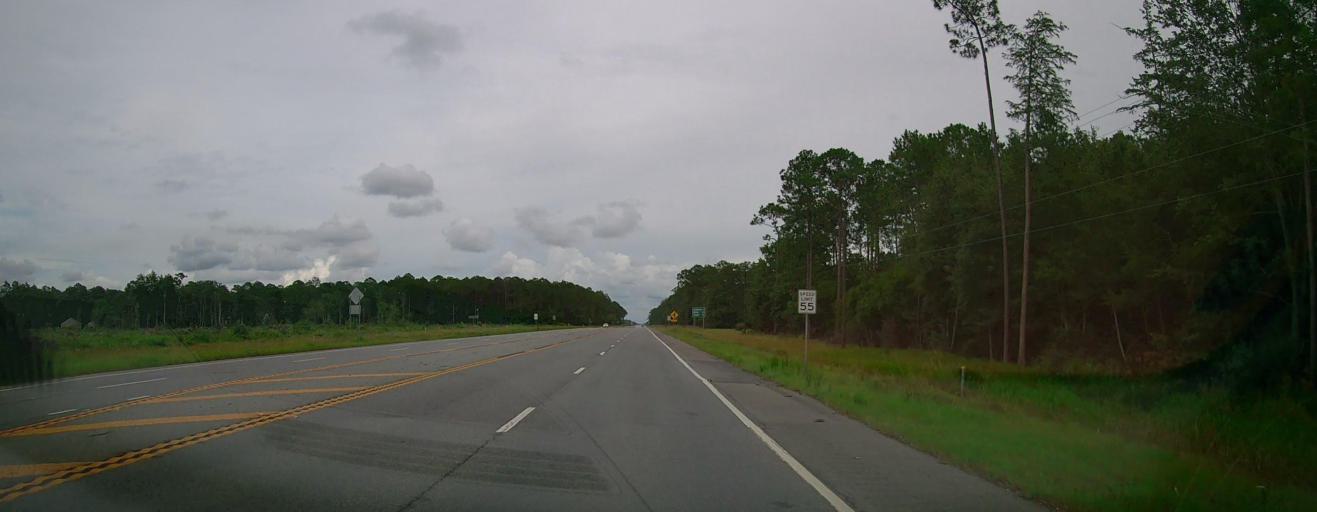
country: US
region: Georgia
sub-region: Appling County
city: Baxley
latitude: 31.7659
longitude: -82.3121
